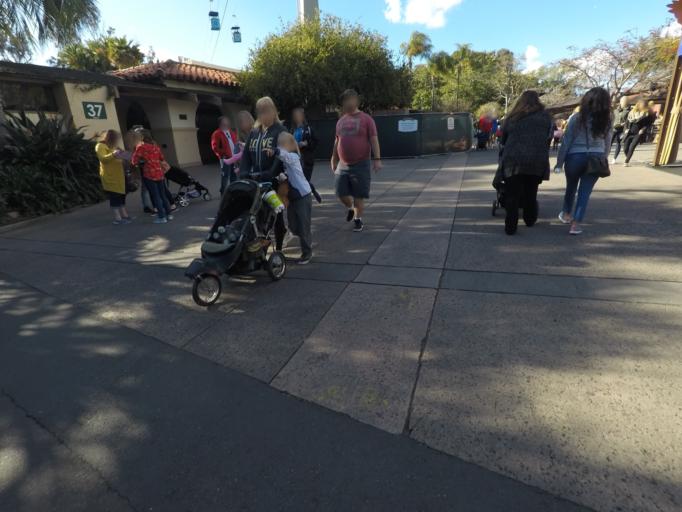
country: US
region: California
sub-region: San Diego County
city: San Diego
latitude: 32.7340
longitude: -117.1492
